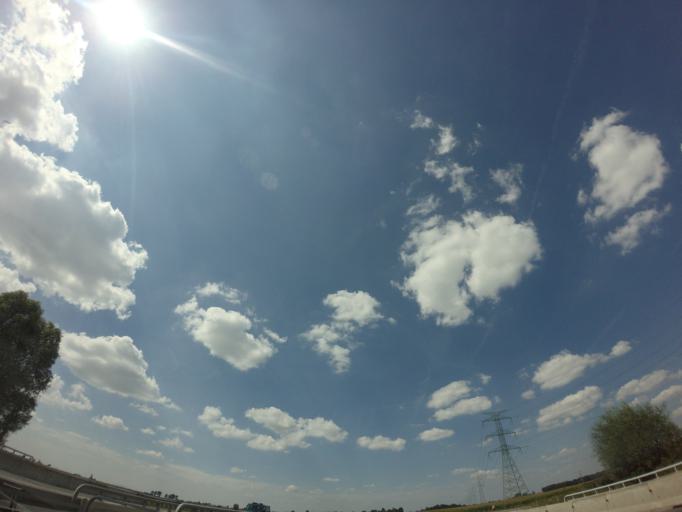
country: PL
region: Lower Silesian Voivodeship
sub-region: Powiat strzelinski
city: Wiazow
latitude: 50.8514
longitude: 17.2348
